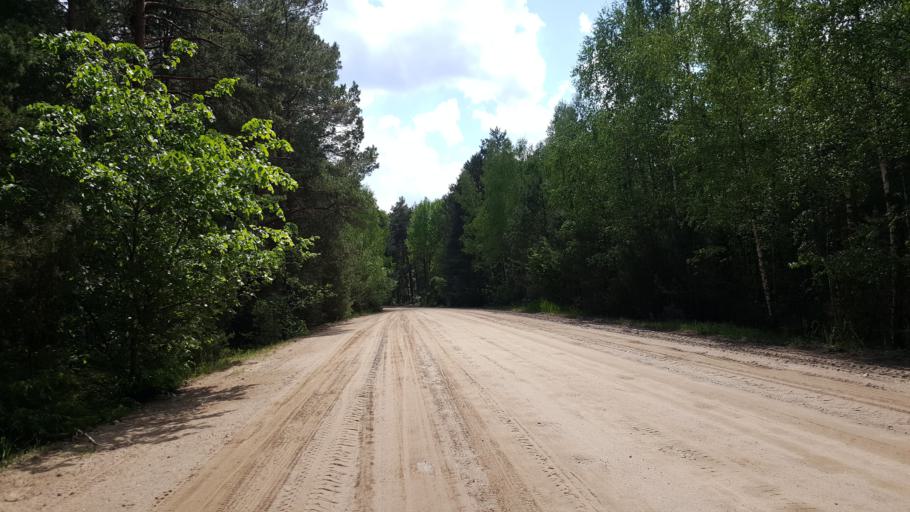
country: BY
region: Brest
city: Kamyanyets
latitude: 52.4379
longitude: 23.9739
